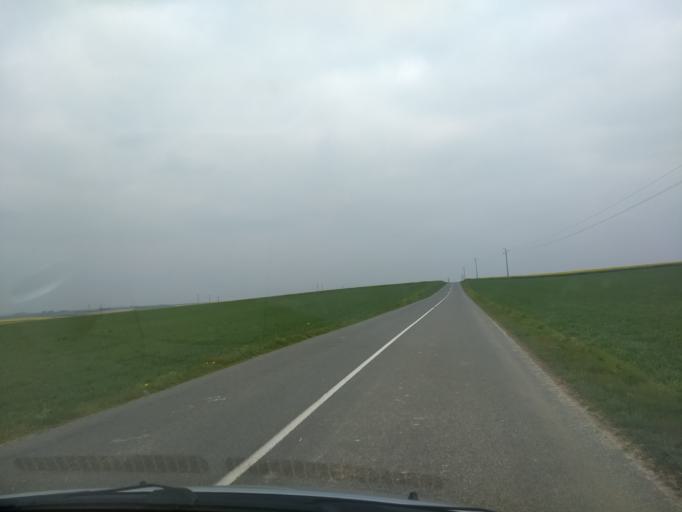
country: FR
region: Nord-Pas-de-Calais
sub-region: Departement du Pas-de-Calais
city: Mont-Saint-Eloi
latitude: 50.3514
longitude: 2.7149
